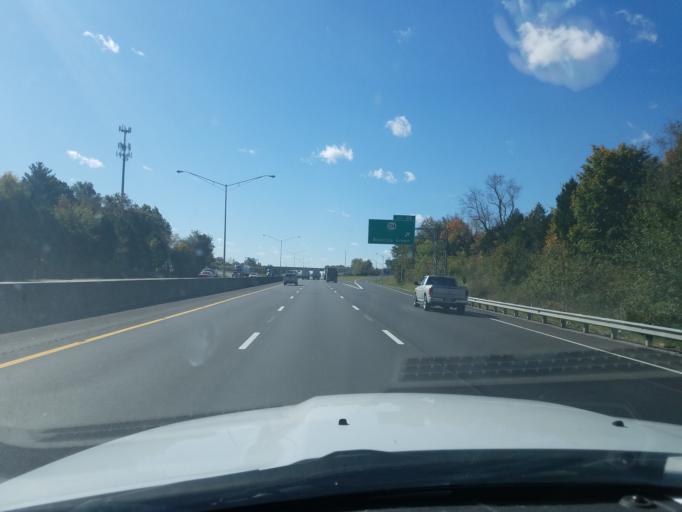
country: US
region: Kentucky
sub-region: Warren County
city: Bowling Green
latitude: 36.9820
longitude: -86.3888
